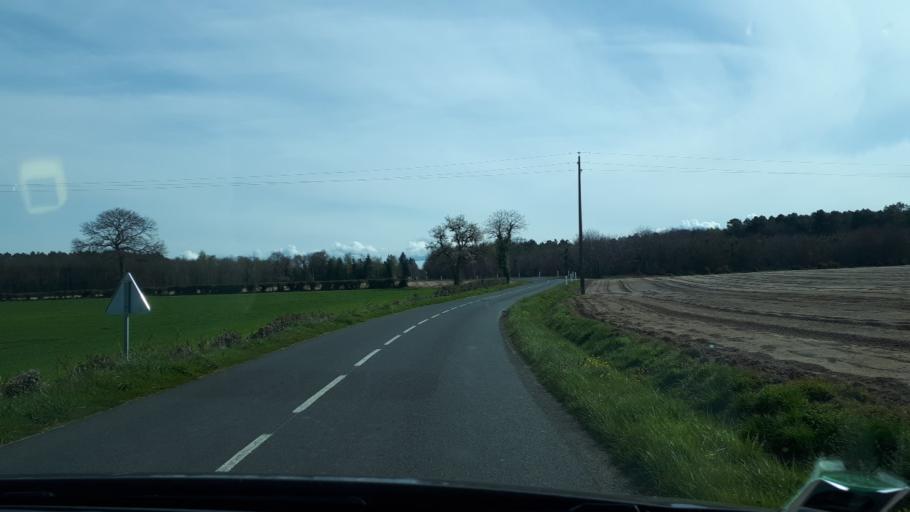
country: FR
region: Pays de la Loire
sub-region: Departement de la Sarthe
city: Yvre-le-Polin
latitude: 47.8165
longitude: 0.1327
